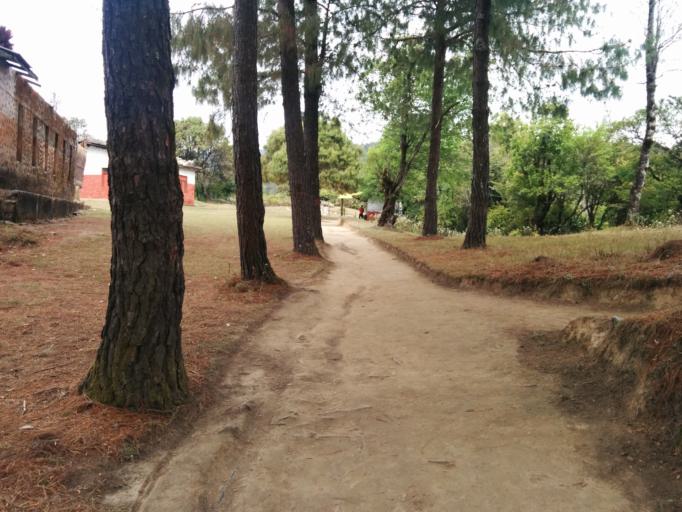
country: NP
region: Central Region
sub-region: Bagmati Zone
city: Nagarkot
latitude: 27.7844
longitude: 85.4351
